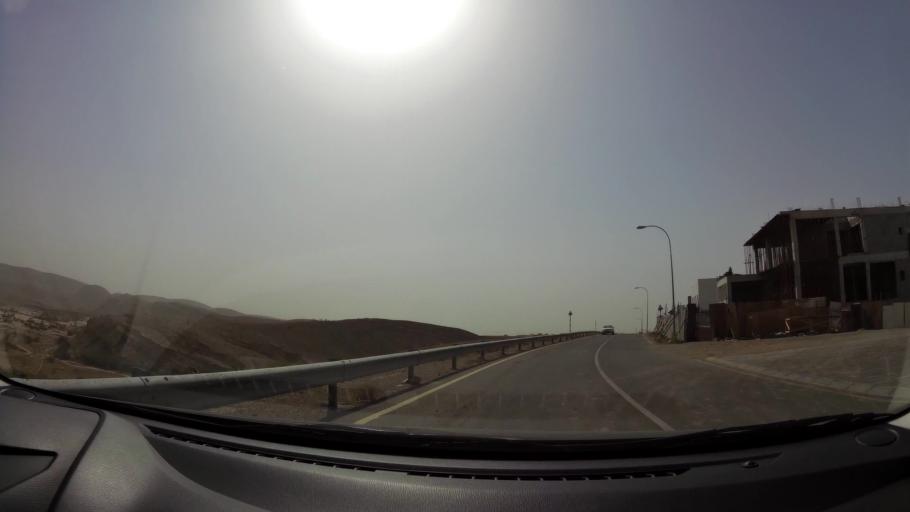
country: OM
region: Muhafazat Masqat
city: Bawshar
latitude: 23.5514
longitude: 58.3446
